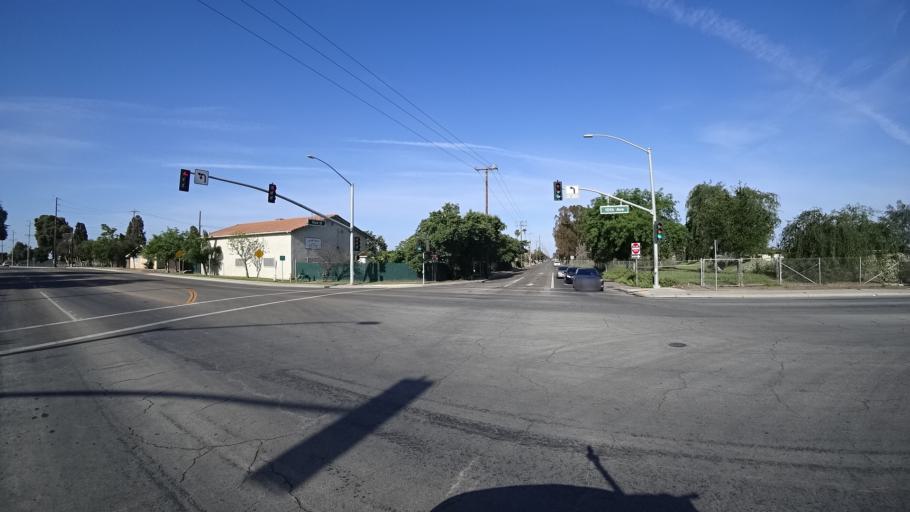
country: US
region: California
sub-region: Kings County
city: Hanford
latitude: 36.3237
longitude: -119.6369
